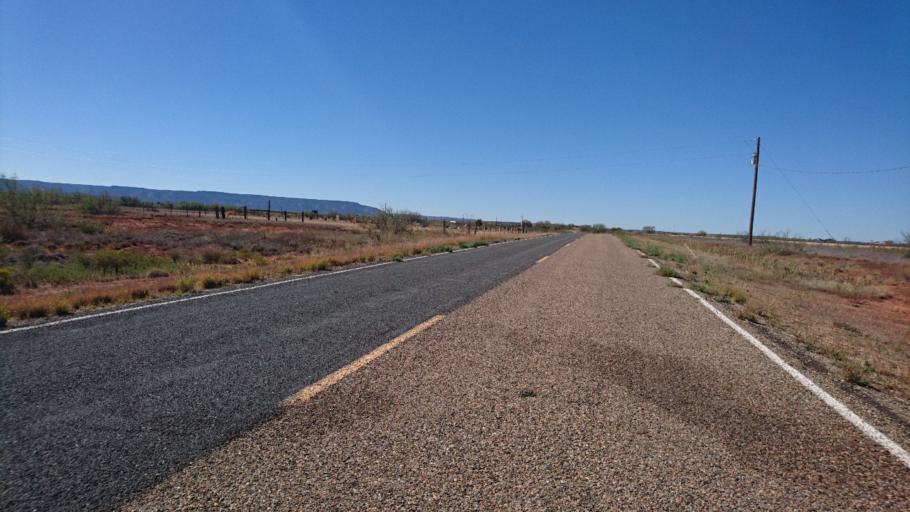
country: US
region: New Mexico
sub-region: Quay County
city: Tucumcari
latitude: 35.0992
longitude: -104.0539
